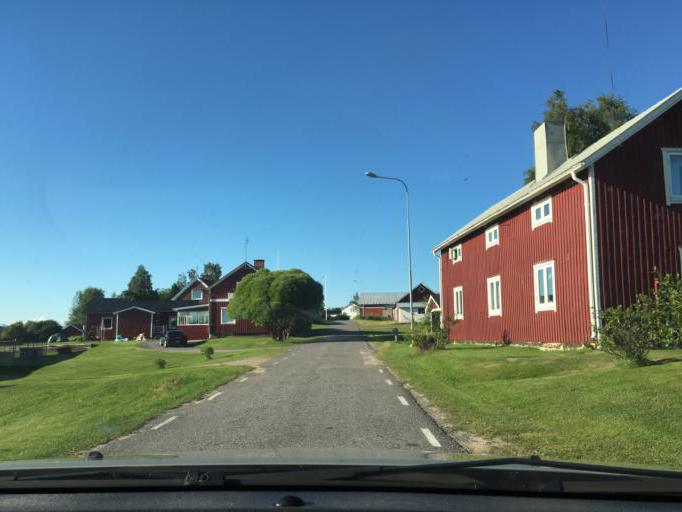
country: SE
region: Norrbotten
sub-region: Overkalix Kommun
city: OEverkalix
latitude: 66.1051
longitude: 22.7822
